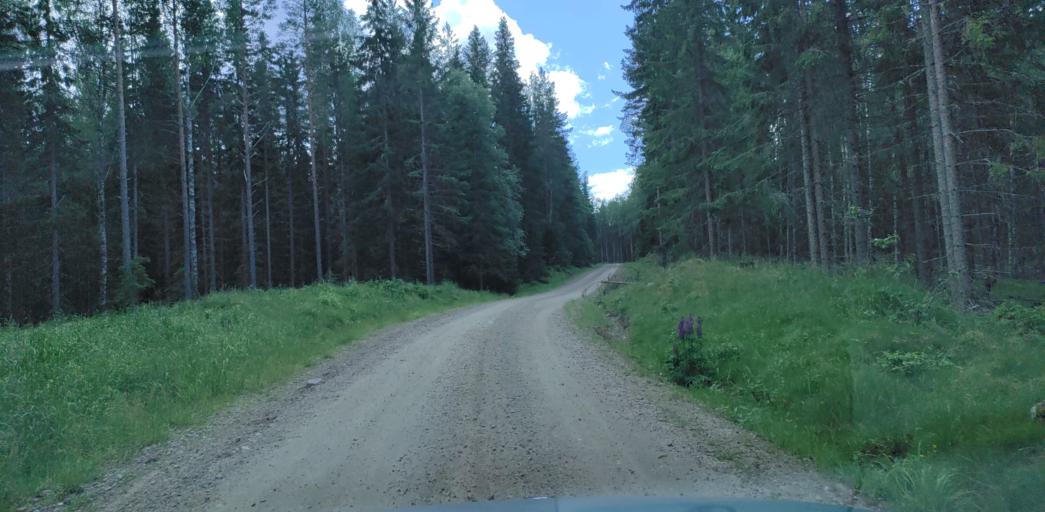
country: SE
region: Vaermland
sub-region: Hagfors Kommun
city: Ekshaerad
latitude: 60.0556
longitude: 13.3105
